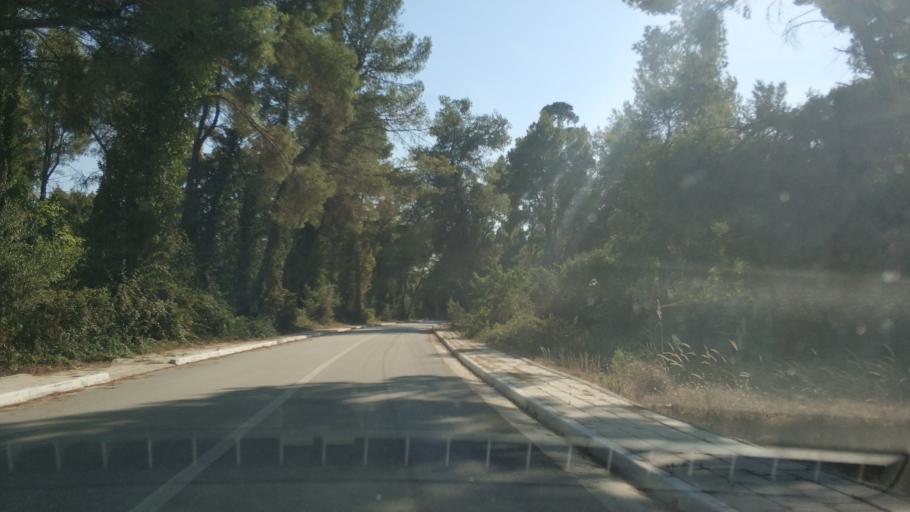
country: AL
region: Fier
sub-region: Rrethi i Lushnjes
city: Divjake
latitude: 40.9656
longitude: 19.4781
